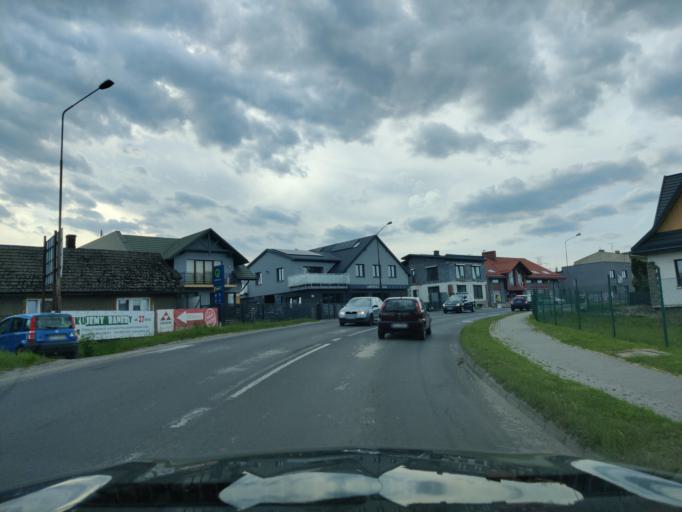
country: PL
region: Silesian Voivodeship
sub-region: Powiat zywiecki
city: Zywiec
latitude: 49.6864
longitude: 19.1844
